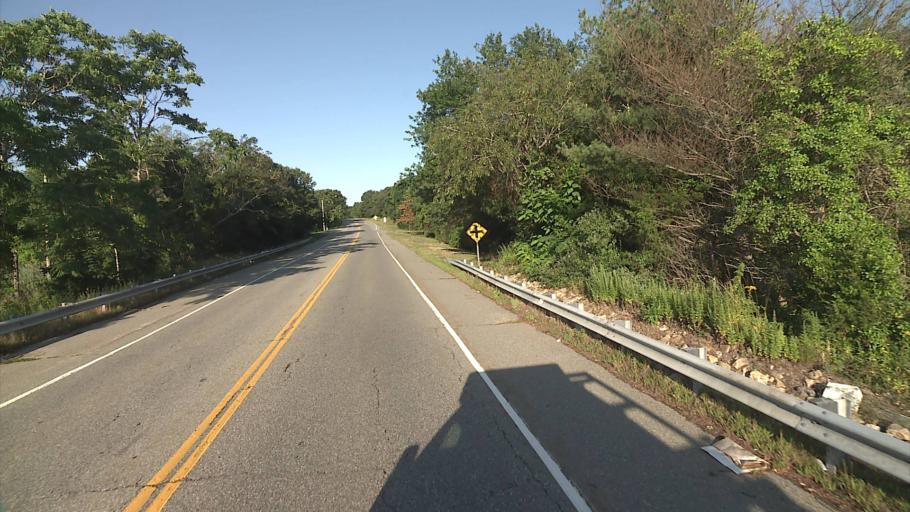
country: US
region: Connecticut
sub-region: New London County
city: Mystic
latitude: 41.3472
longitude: -71.9207
